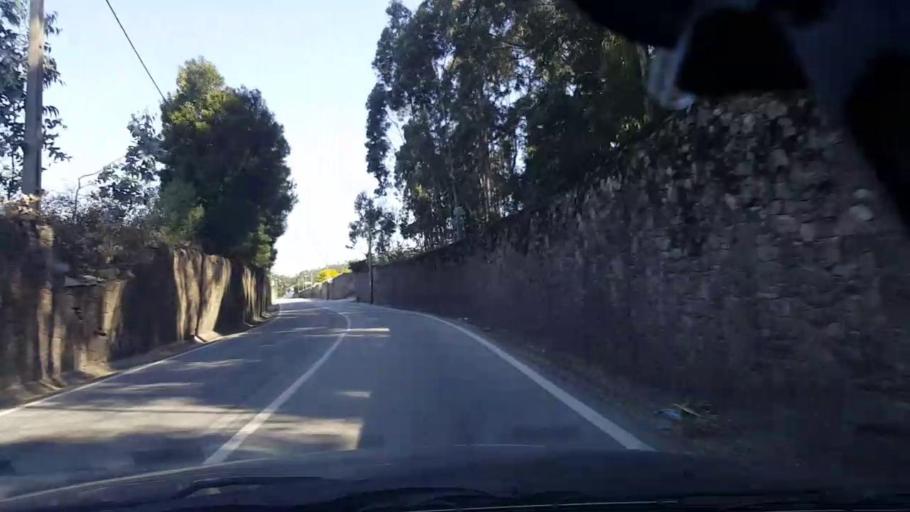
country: PT
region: Porto
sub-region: Vila do Conde
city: Arvore
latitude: 41.3673
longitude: -8.6691
